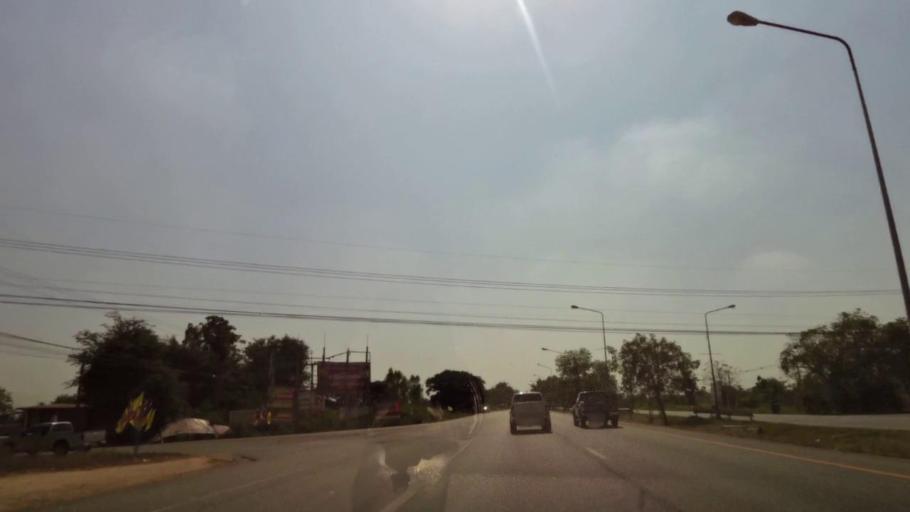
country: TH
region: Phichit
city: Wachira Barami
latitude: 16.4107
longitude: 100.1428
